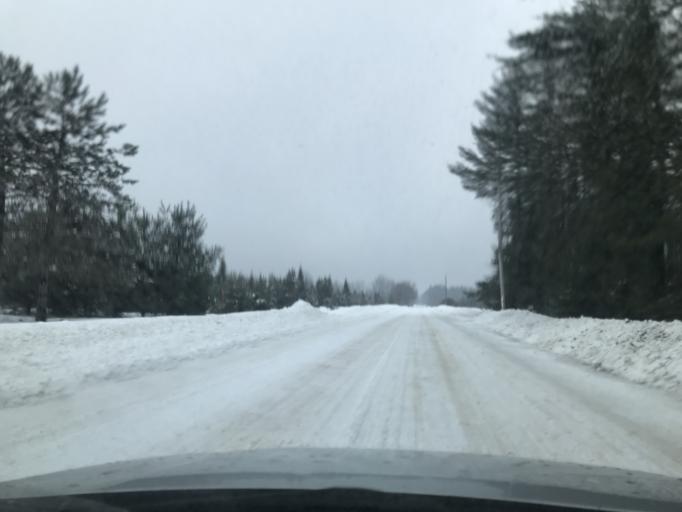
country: US
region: Wisconsin
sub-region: Marinette County
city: Peshtigo
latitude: 45.3812
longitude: -87.9324
